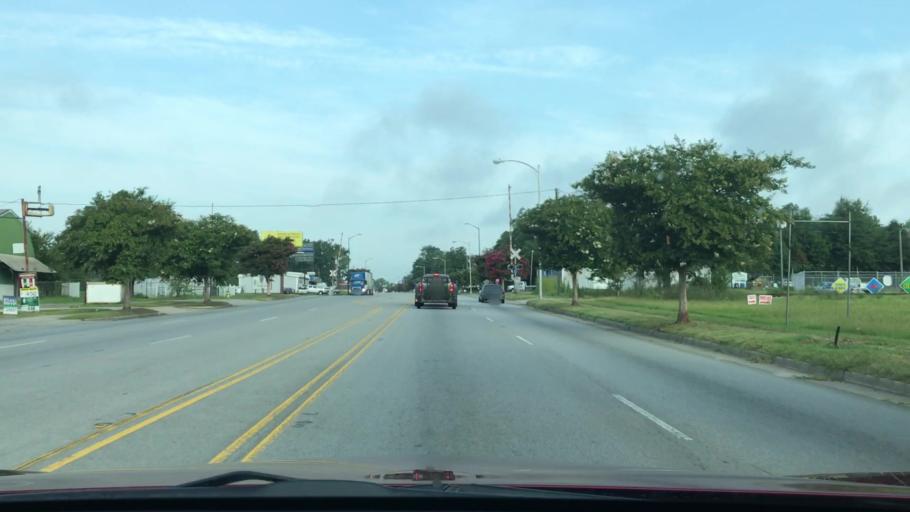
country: US
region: South Carolina
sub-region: Orangeburg County
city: Orangeburg
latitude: 33.4898
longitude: -80.8450
